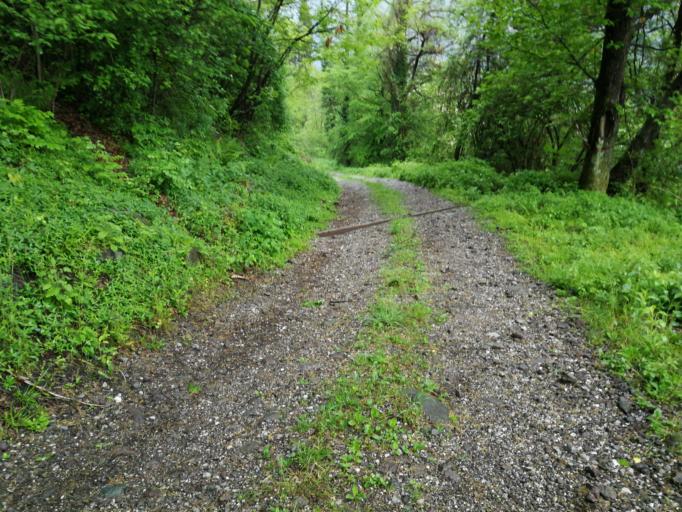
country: IT
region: Trentino-Alto Adige
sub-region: Provincia di Trento
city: Condino
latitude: 45.8782
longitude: 10.5829
